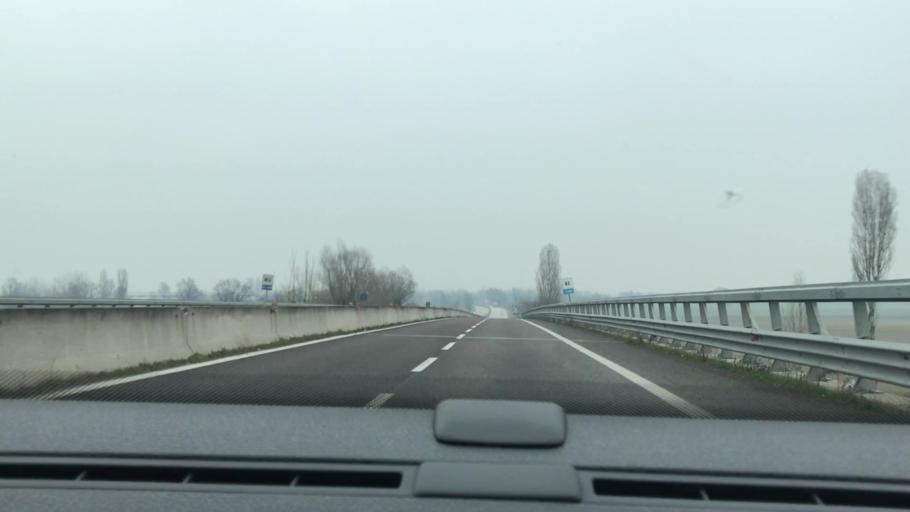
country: IT
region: Veneto
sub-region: Provincia di Rovigo
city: Grignano Polesine
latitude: 45.0252
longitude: 11.7596
